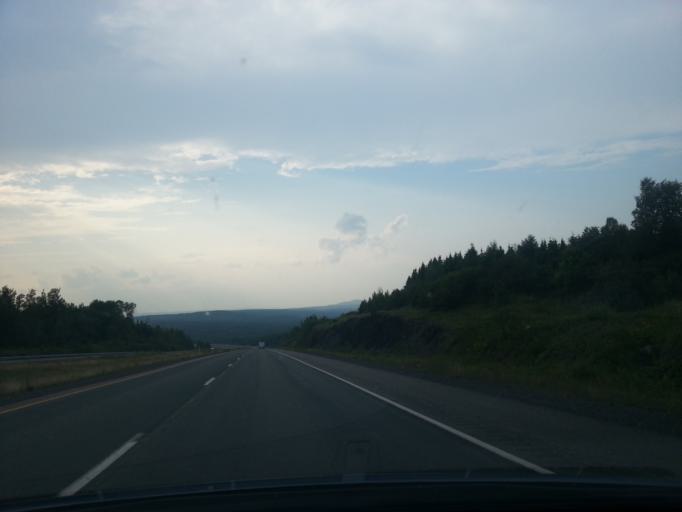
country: CA
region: New Brunswick
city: Harrison Brook
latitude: 47.2800
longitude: -68.0226
